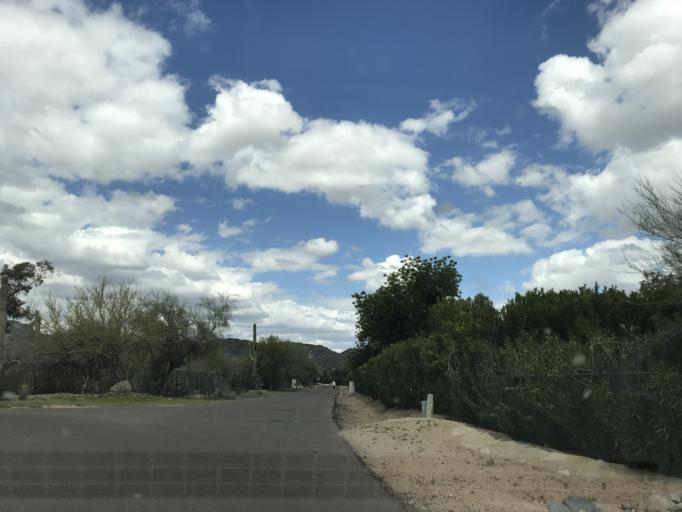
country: US
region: Arizona
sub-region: Maricopa County
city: Paradise Valley
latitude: 33.5217
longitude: -111.9454
